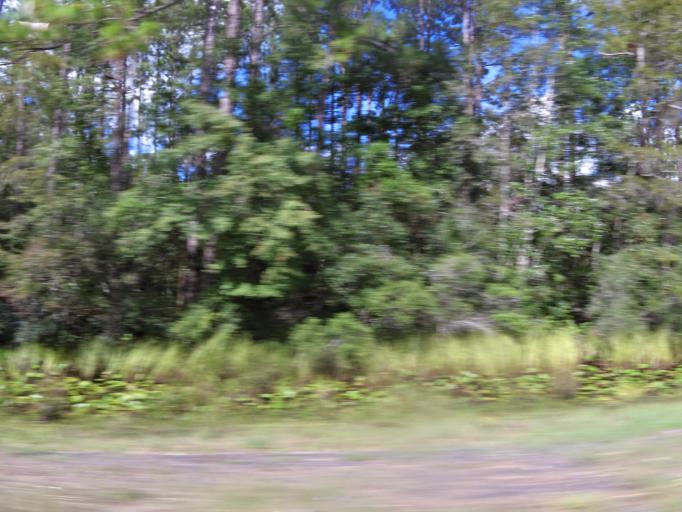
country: US
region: Florida
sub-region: Hamilton County
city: Jasper
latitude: 30.6748
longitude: -82.6780
